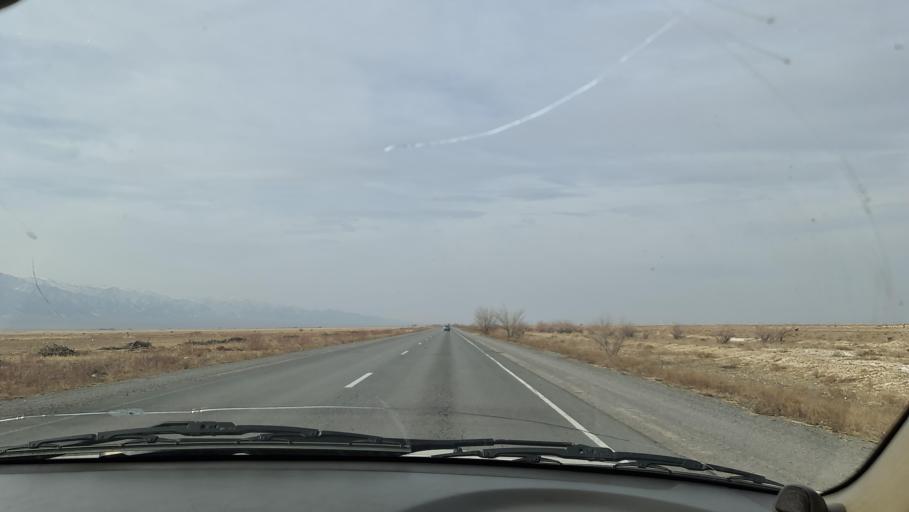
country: KG
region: Chuy
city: Tokmok
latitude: 43.3416
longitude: 75.5509
